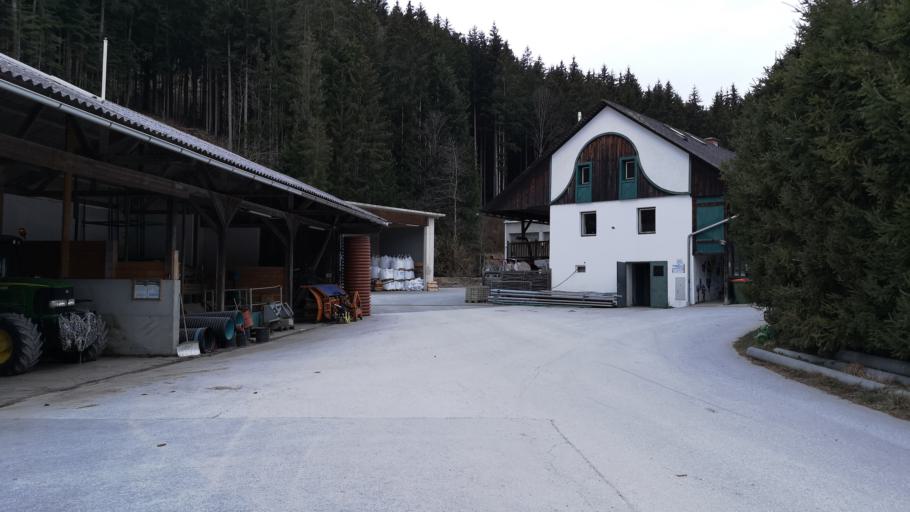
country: AT
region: Styria
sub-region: Politischer Bezirk Weiz
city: Birkfeld
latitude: 47.3589
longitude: 15.6882
